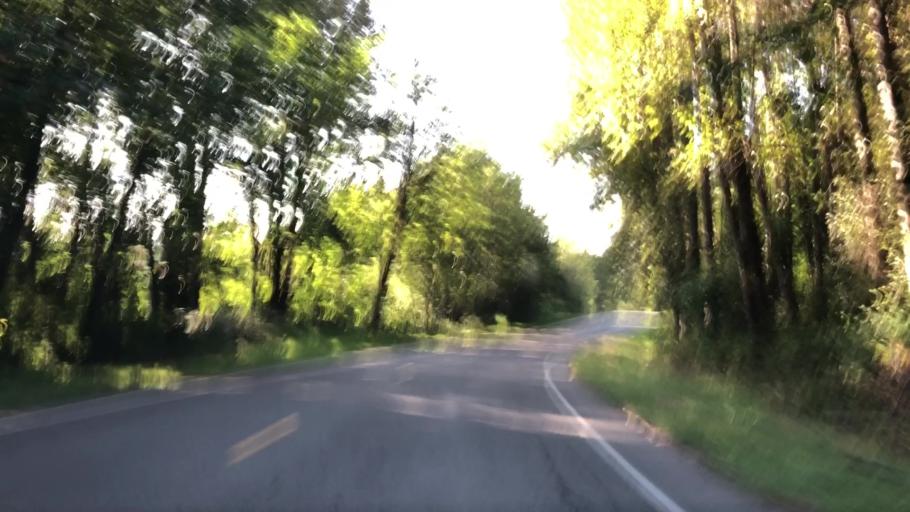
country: US
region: Washington
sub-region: King County
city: Woodinville
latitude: 47.7666
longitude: -122.1749
